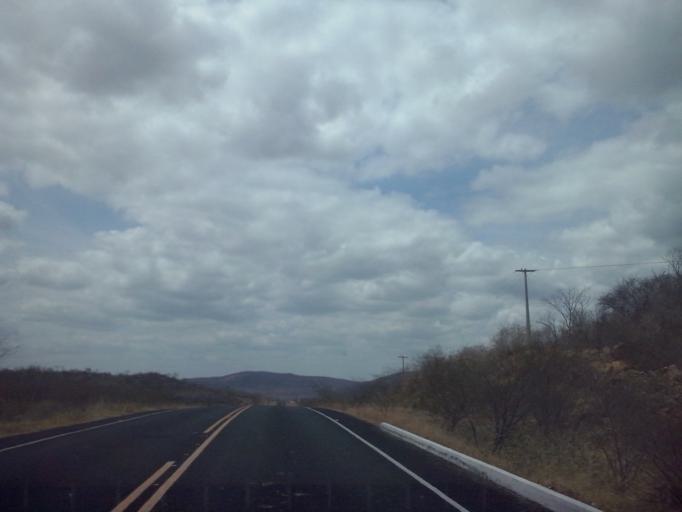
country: BR
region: Paraiba
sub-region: Patos
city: Patos
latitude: -6.8834
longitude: -37.5315
